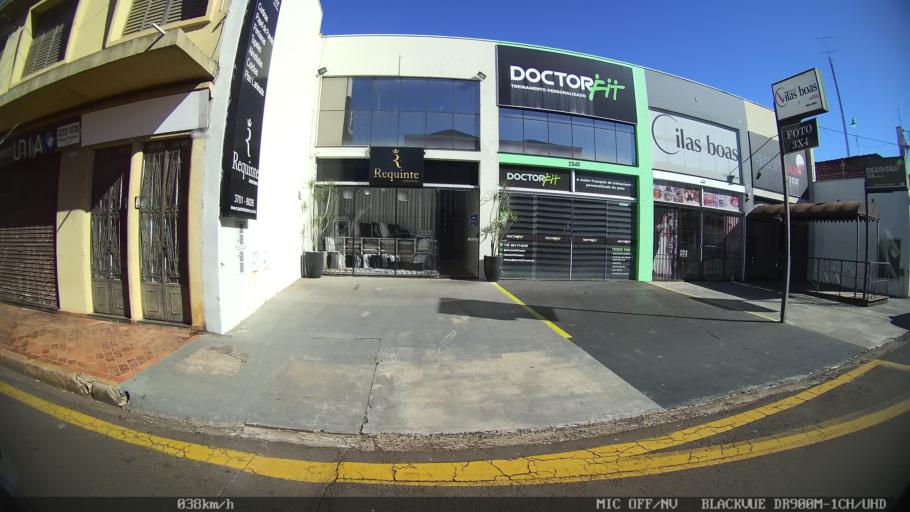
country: BR
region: Sao Paulo
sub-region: Franca
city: Franca
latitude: -20.5334
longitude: -47.3978
